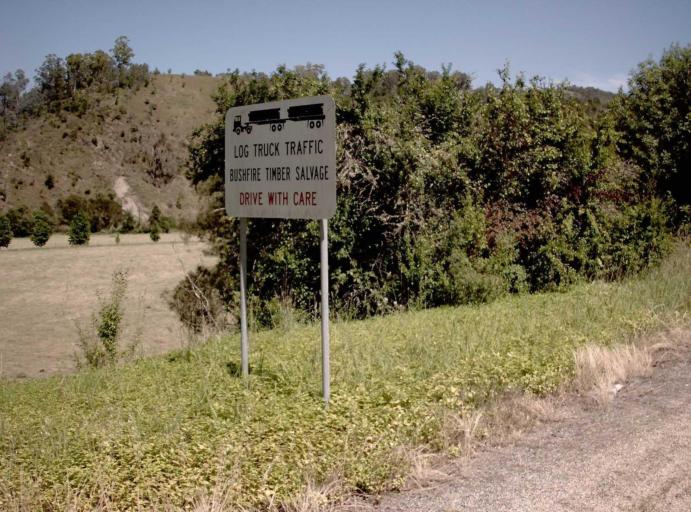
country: AU
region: Victoria
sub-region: East Gippsland
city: Lakes Entrance
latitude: -37.4931
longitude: 148.1733
